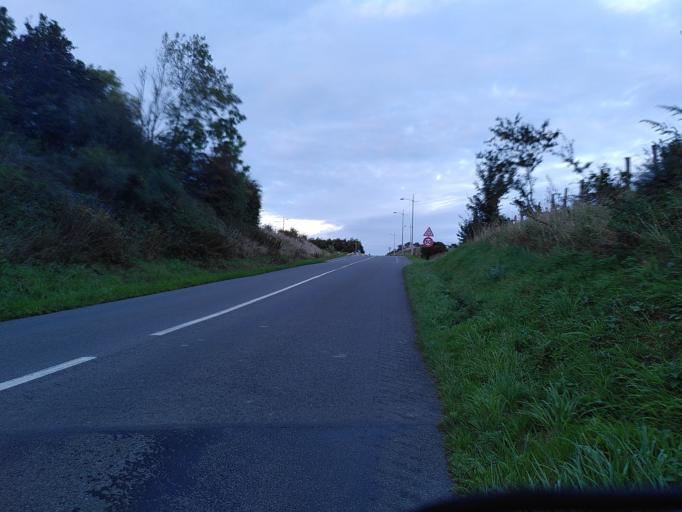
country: FR
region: Nord-Pas-de-Calais
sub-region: Departement du Pas-de-Calais
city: Therouanne
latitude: 50.6442
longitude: 2.2662
